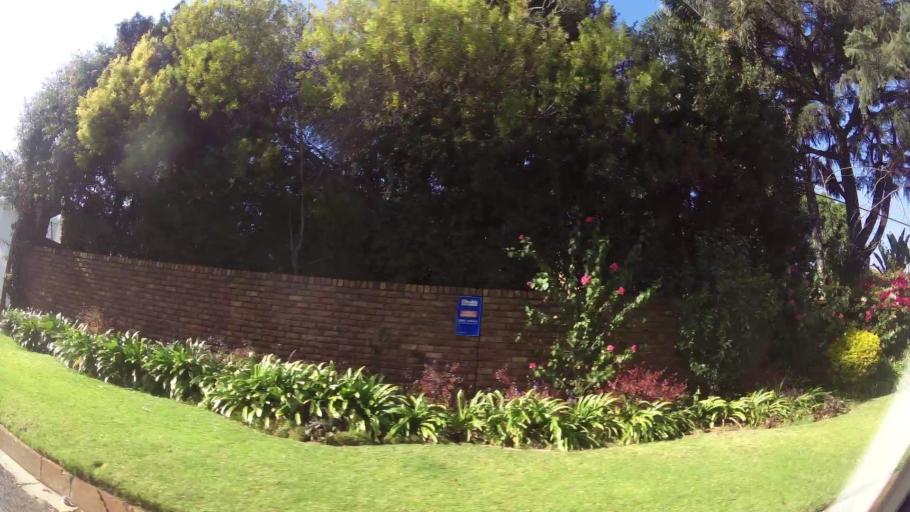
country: ZA
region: Gauteng
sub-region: Ekurhuleni Metropolitan Municipality
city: Germiston
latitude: -26.1775
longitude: 28.1481
